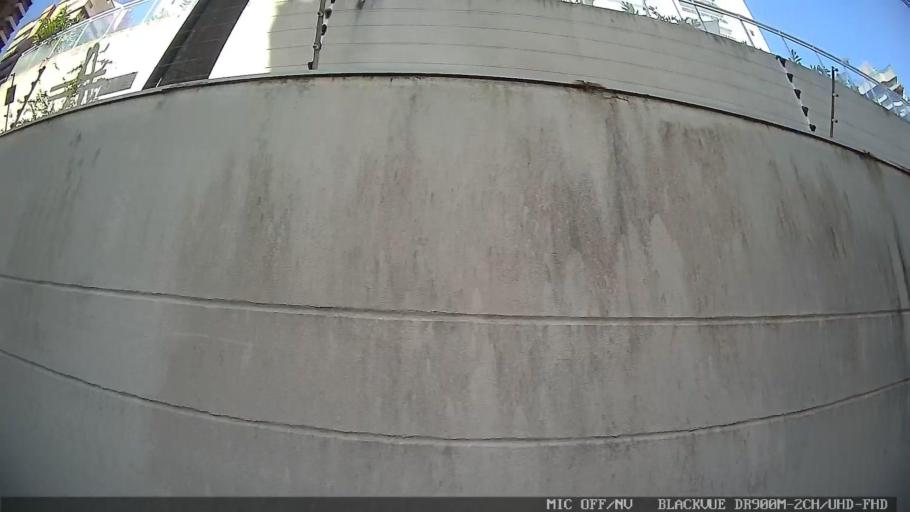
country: BR
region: Sao Paulo
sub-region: Guaruja
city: Guaruja
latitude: -24.0062
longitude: -46.2704
